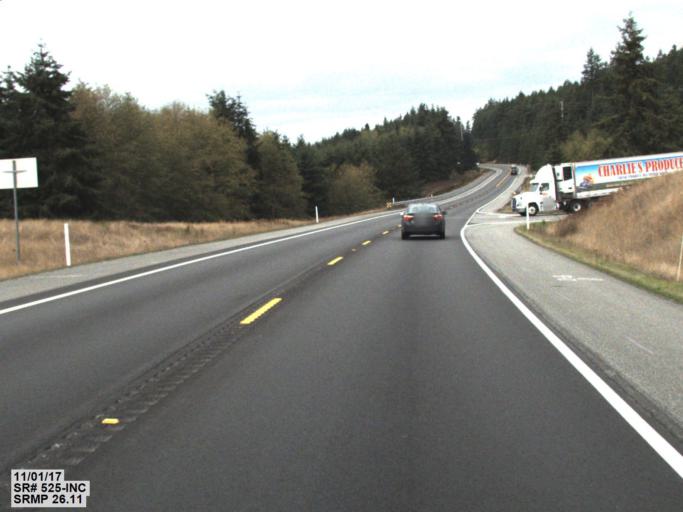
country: US
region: Washington
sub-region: Island County
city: Camano
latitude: 48.1115
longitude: -122.5831
